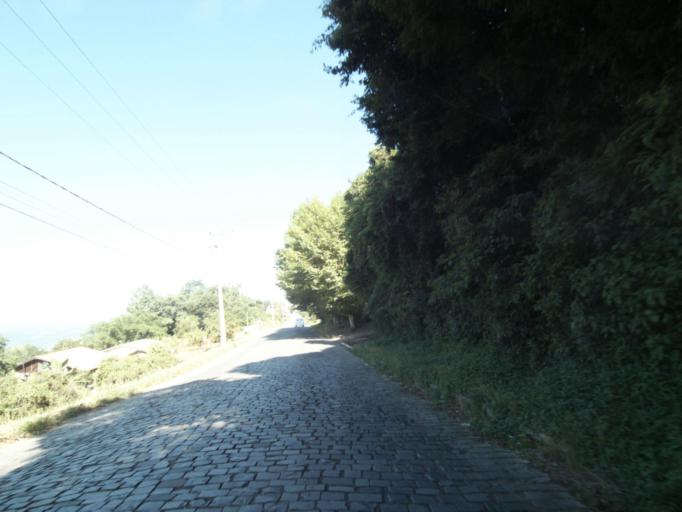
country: BR
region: Rio Grande do Sul
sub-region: Bento Goncalves
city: Bento Goncalves
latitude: -29.1186
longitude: -51.5661
